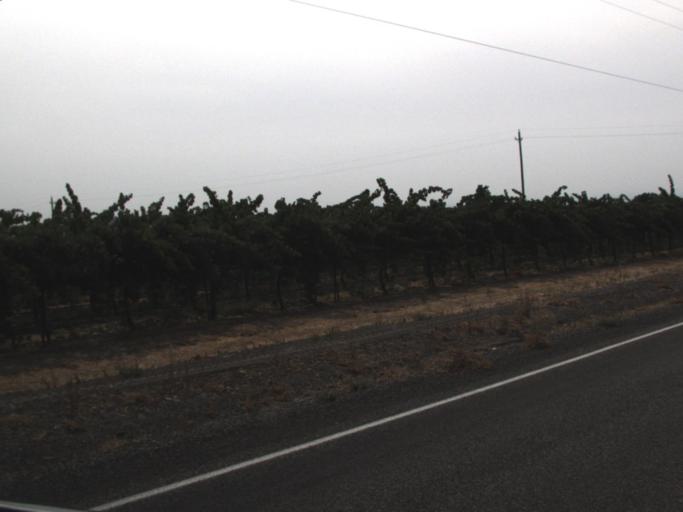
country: US
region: Washington
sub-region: Yakima County
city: Sunnyside
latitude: 46.3835
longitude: -119.9630
